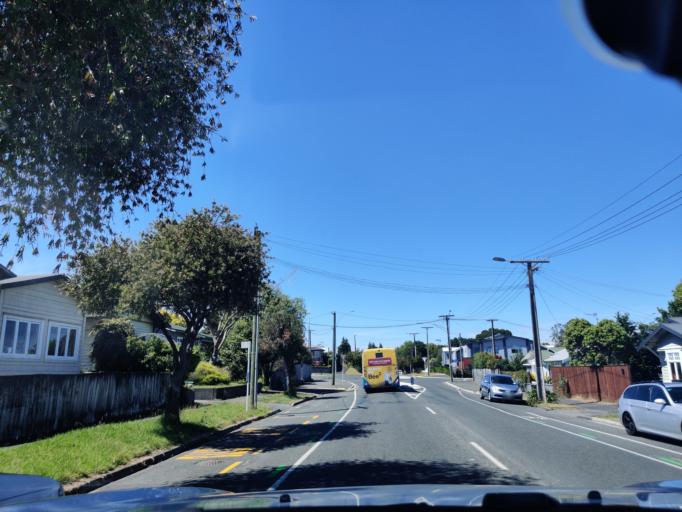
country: NZ
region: Waikato
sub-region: Hamilton City
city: Hamilton
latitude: -37.7941
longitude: 175.2675
